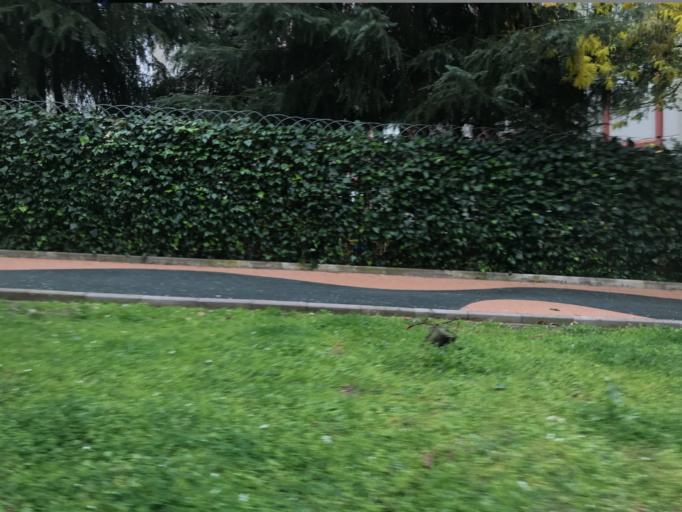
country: TR
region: Istanbul
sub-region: Atasehir
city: Atasehir
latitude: 40.9897
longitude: 29.1330
